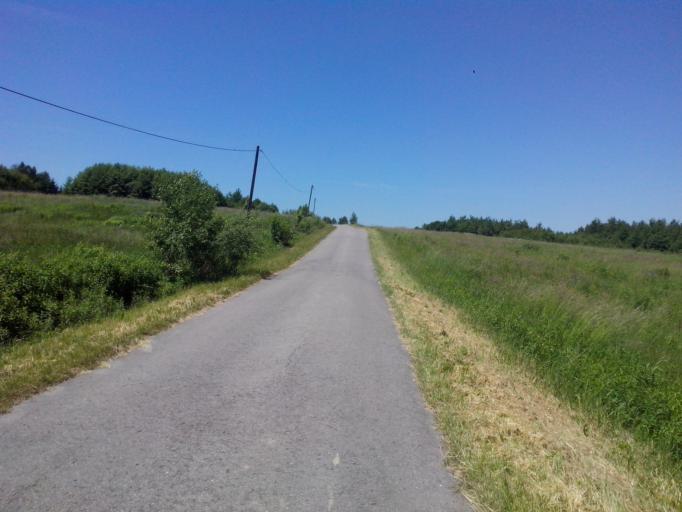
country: PL
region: Subcarpathian Voivodeship
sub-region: Powiat strzyzowski
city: Wysoka Strzyzowska
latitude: 49.8197
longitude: 21.7590
